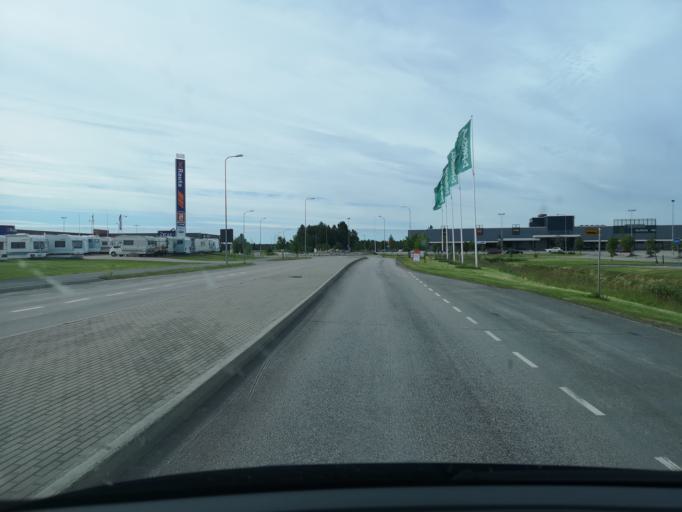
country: FI
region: Northern Ostrobothnia
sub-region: Ylivieska
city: Ylivieska
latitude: 64.0623
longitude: 24.5596
